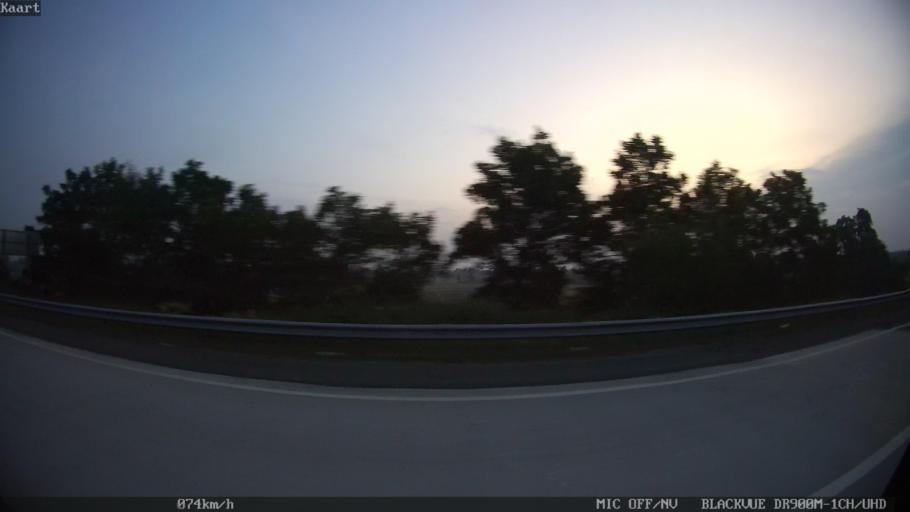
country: ID
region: Lampung
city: Sidorejo
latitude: -5.5664
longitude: 105.5349
